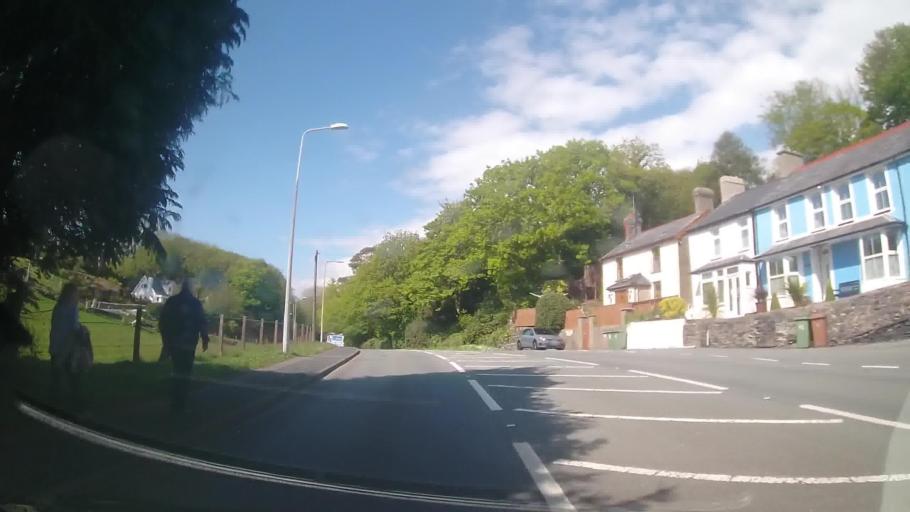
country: GB
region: Wales
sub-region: Gwynedd
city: Porthmadog
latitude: 52.9222
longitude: -4.1342
